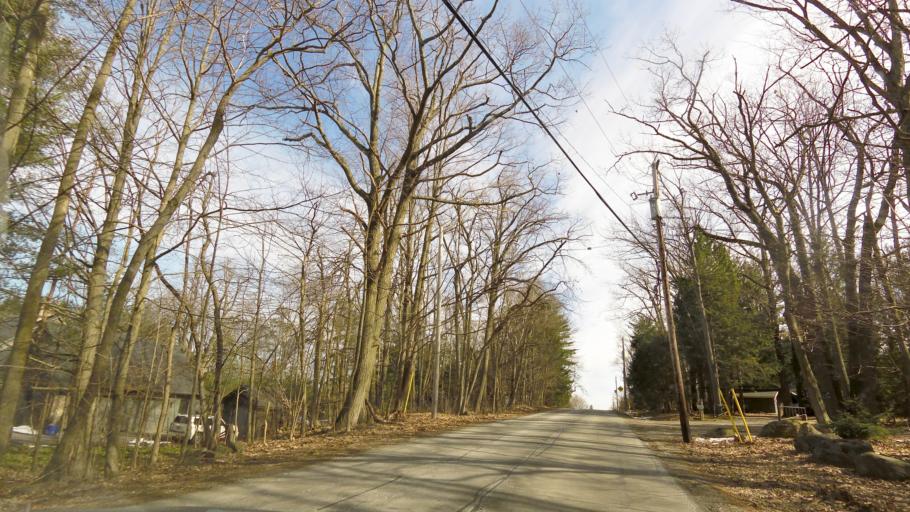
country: CA
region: Ontario
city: Burlington
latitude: 43.4032
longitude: -79.9665
